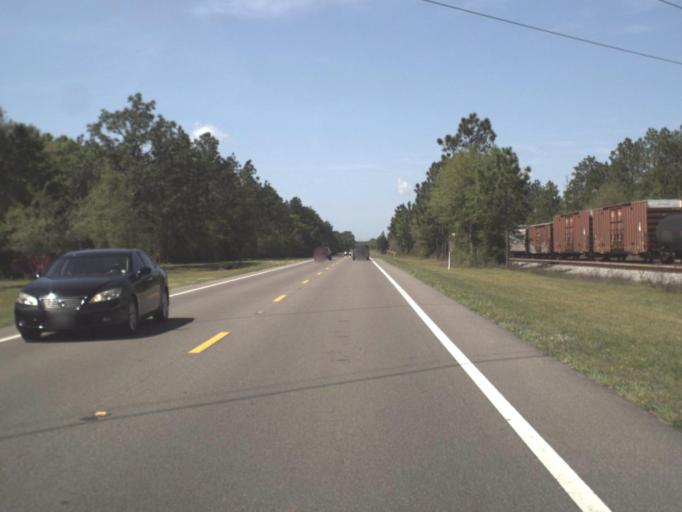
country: US
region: Florida
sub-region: Santa Rosa County
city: East Milton
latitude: 30.6677
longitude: -86.8677
